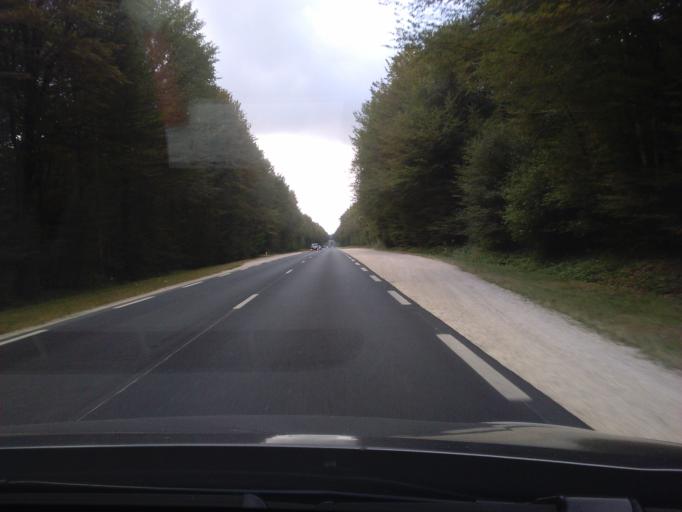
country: FR
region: Centre
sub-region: Departement du Loir-et-Cher
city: Cellettes
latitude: 47.5502
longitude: 1.3743
